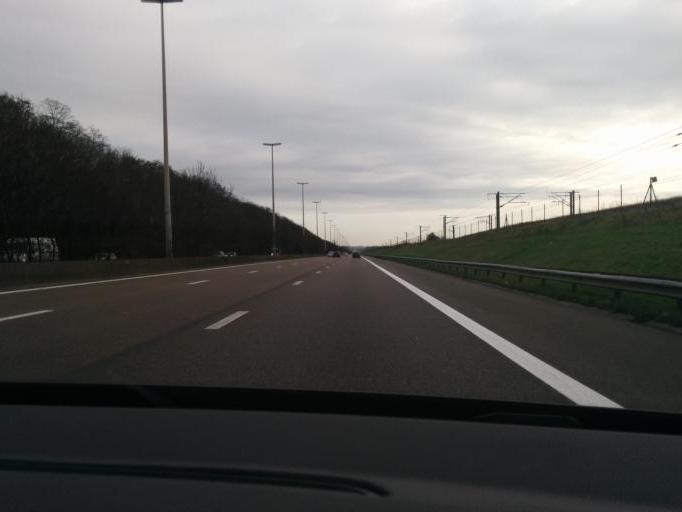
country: BE
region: Flanders
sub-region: Provincie Vlaams-Brabant
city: Boutersem
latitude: 50.8115
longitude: 4.8613
